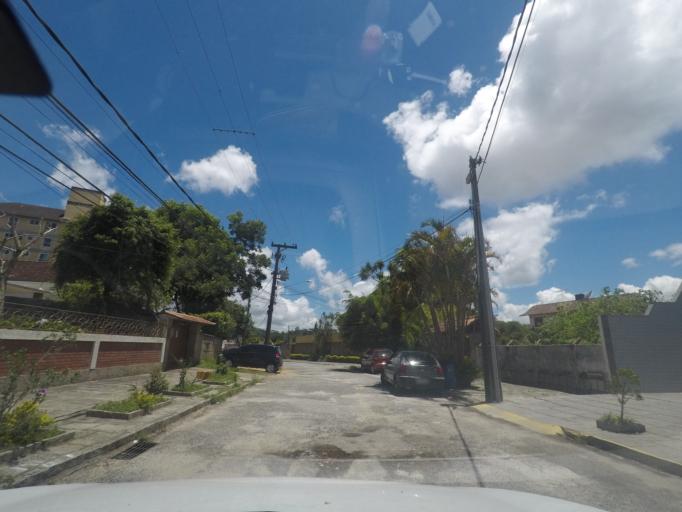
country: BR
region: Rio de Janeiro
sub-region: Teresopolis
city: Teresopolis
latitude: -22.4323
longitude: -42.9798
